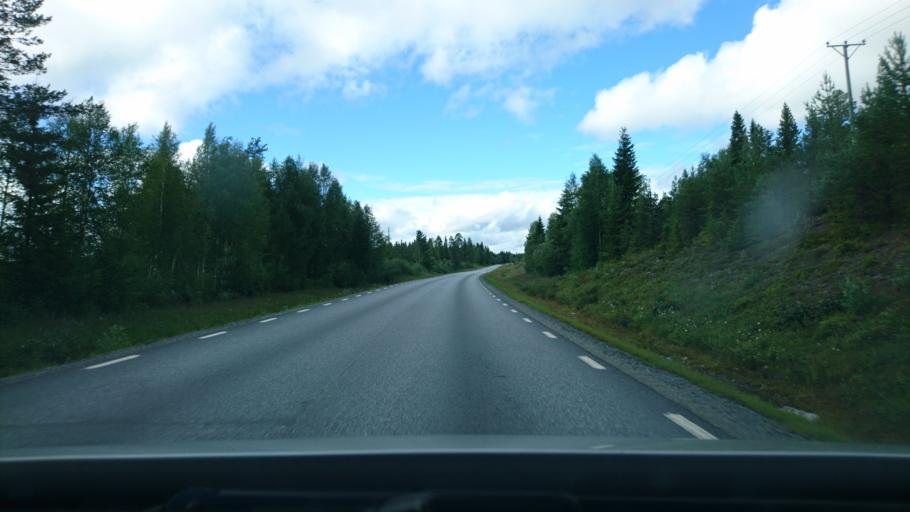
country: SE
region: Vaesterbotten
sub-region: Vilhelmina Kommun
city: Vilhelmina
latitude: 64.5497
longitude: 16.7423
